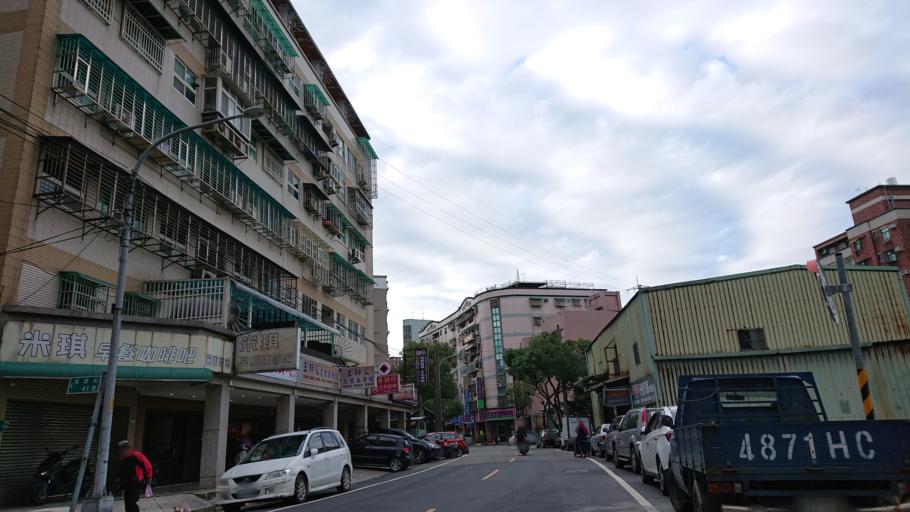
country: TW
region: Taiwan
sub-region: Taoyuan
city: Taoyuan
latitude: 24.9328
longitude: 121.3774
